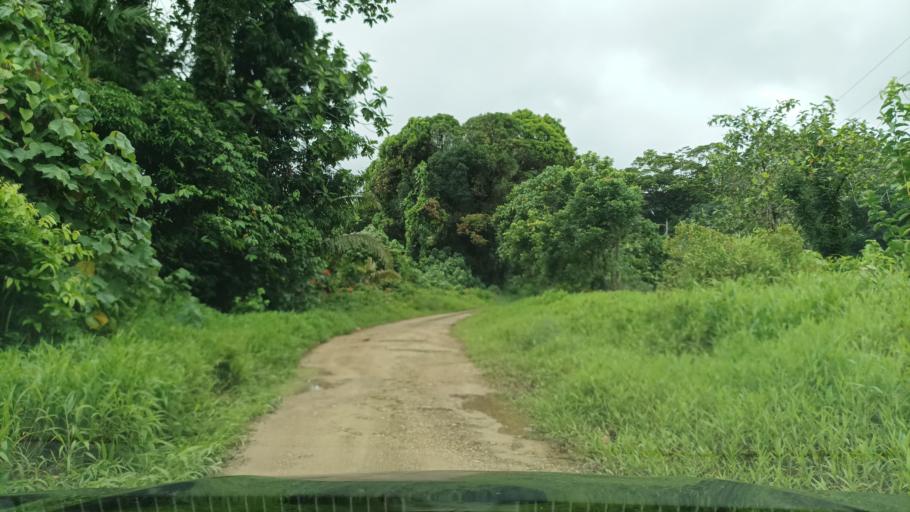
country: FM
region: Pohnpei
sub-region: Madolenihm Municipality
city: Madolenihm Municipality Government
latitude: 6.8194
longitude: 158.2836
